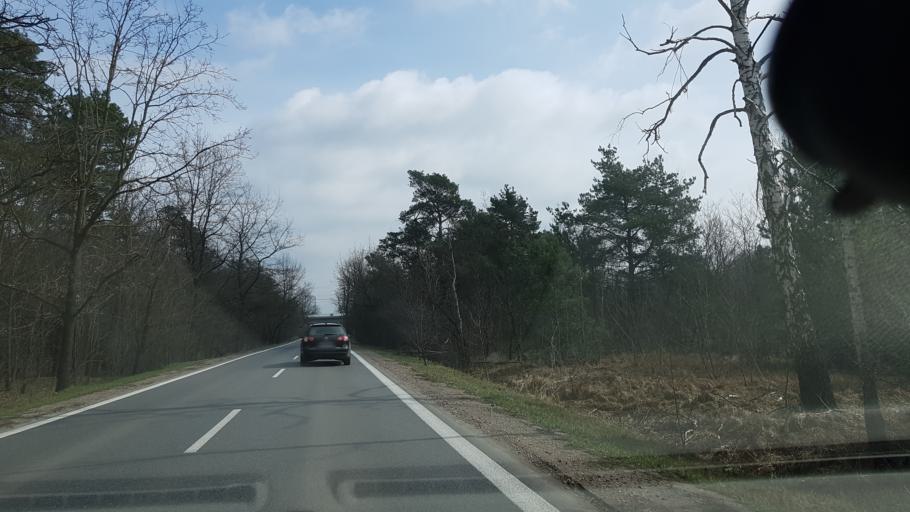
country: PL
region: Masovian Voivodeship
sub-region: Warszawa
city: Rembertow
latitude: 52.2562
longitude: 21.1875
